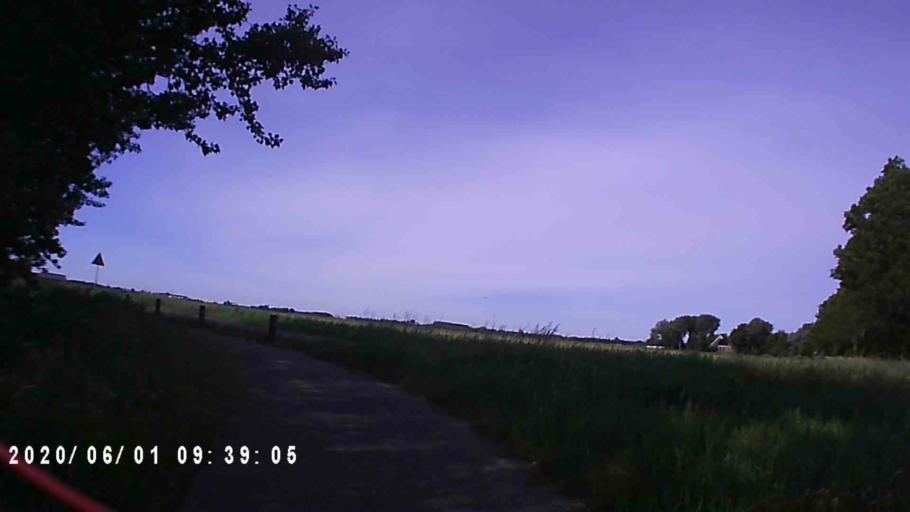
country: NL
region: Friesland
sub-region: Gemeente Het Bildt
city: Sint Annaparochie
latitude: 53.2560
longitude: 5.6806
